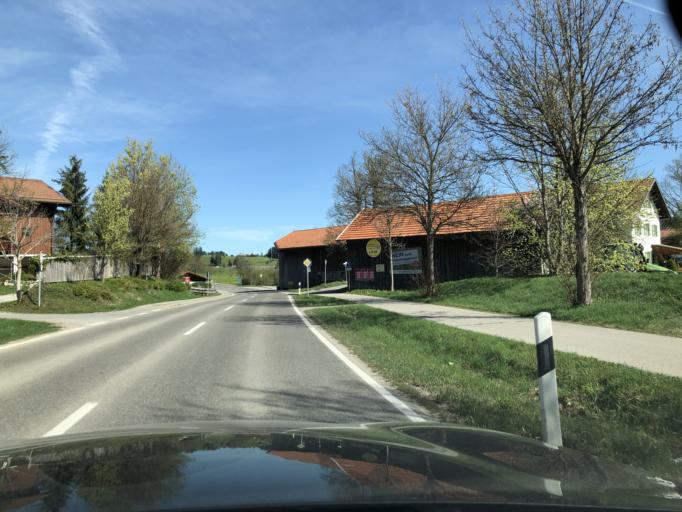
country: DE
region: Bavaria
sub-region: Swabia
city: Eisenberg
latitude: 47.6183
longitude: 10.6092
